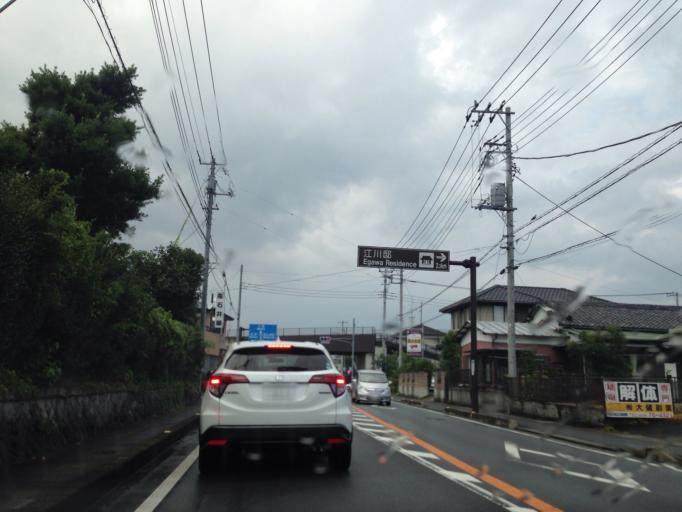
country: JP
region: Shizuoka
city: Mishima
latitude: 35.0550
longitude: 138.9413
